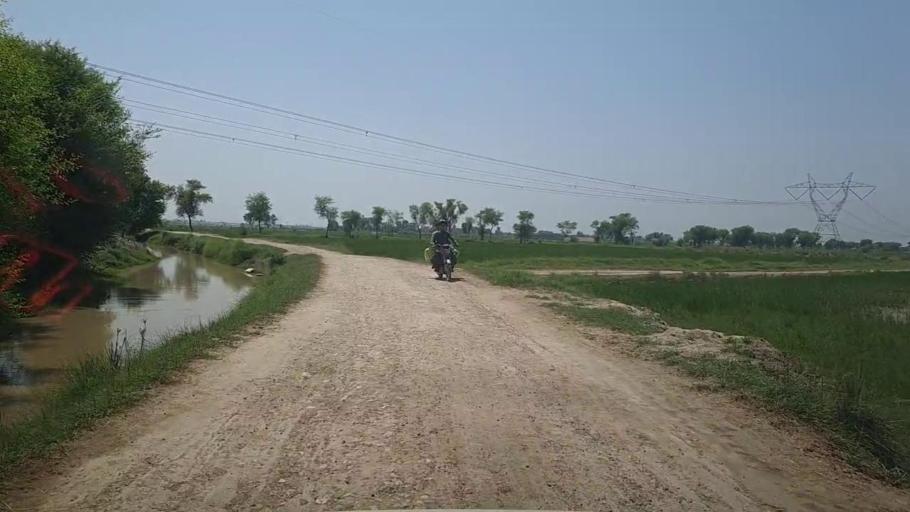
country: PK
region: Sindh
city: Kandhkot
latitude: 28.3249
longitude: 69.3835
